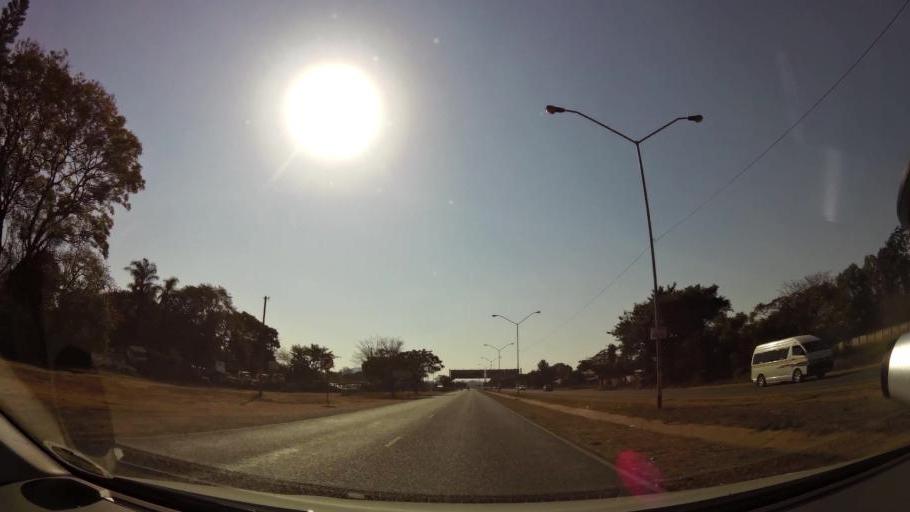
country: ZA
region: Gauteng
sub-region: City of Tshwane Metropolitan Municipality
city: Pretoria
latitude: -25.6716
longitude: 28.1939
